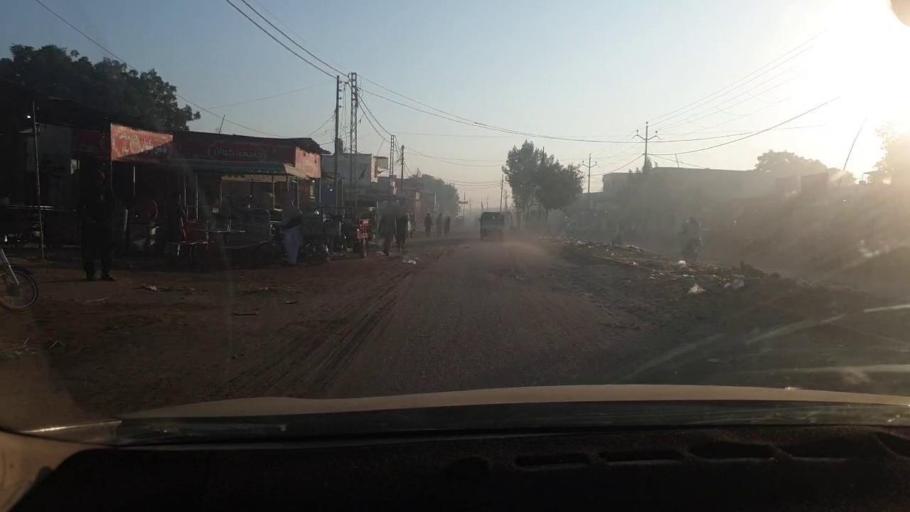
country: PK
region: Sindh
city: Malir Cantonment
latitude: 25.0104
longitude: 67.1616
